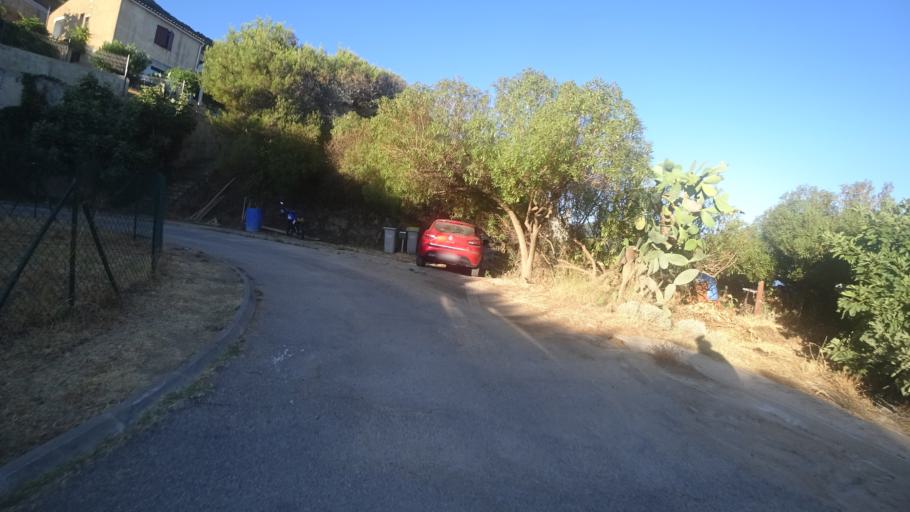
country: FR
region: Corsica
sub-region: Departement de la Corse-du-Sud
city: Alata
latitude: 41.9769
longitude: 8.6641
